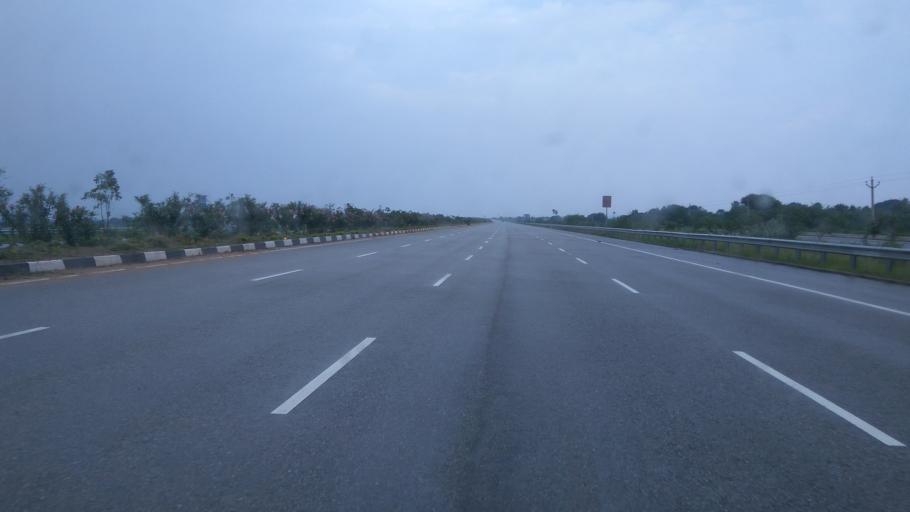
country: IN
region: Telangana
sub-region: Rangareddi
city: Ghatkesar
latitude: 17.4794
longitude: 78.6683
